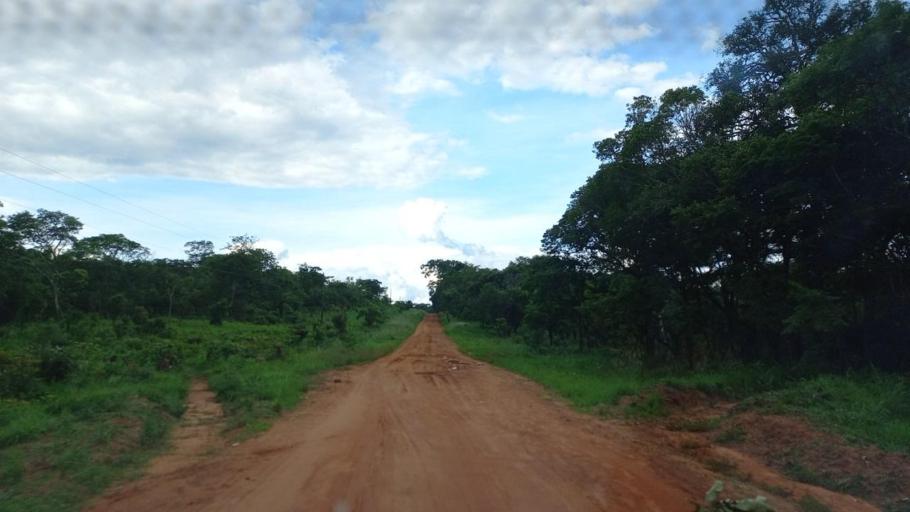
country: ZM
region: North-Western
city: Mwinilunga
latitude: -11.7884
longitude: 24.3729
